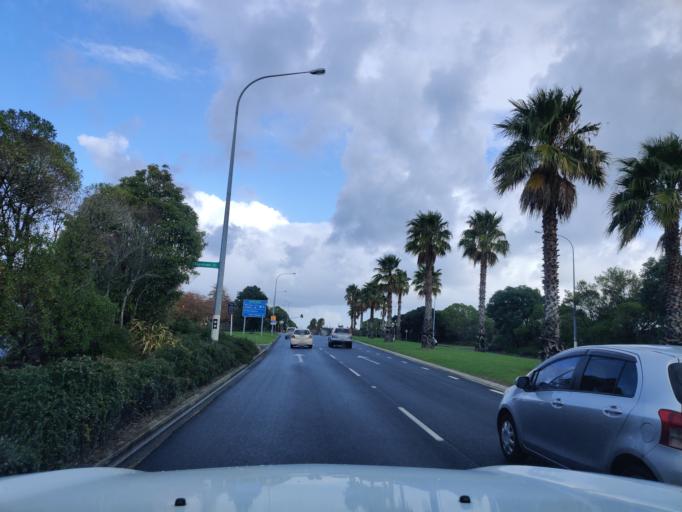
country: NZ
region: Auckland
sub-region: Auckland
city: Pakuranga
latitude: -36.9403
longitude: 174.9090
